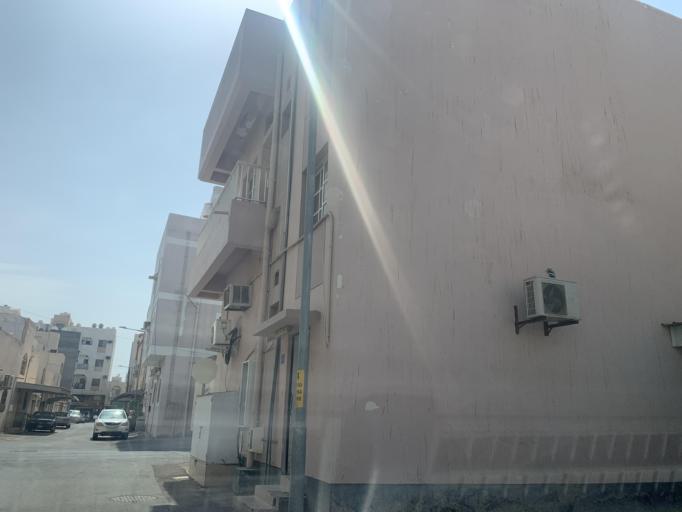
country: BH
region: Muharraq
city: Al Hadd
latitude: 26.2698
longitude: 50.6540
